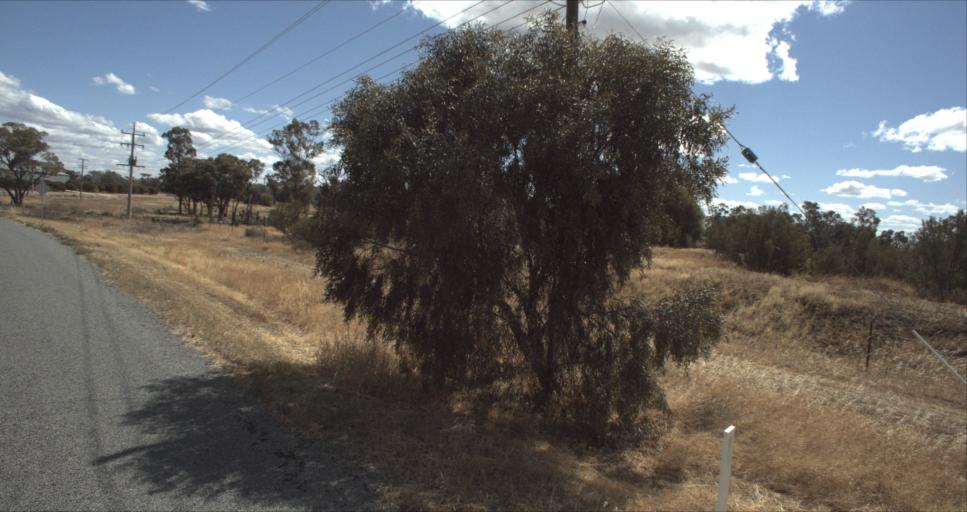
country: AU
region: New South Wales
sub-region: Leeton
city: Leeton
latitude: -34.5172
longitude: 146.2290
